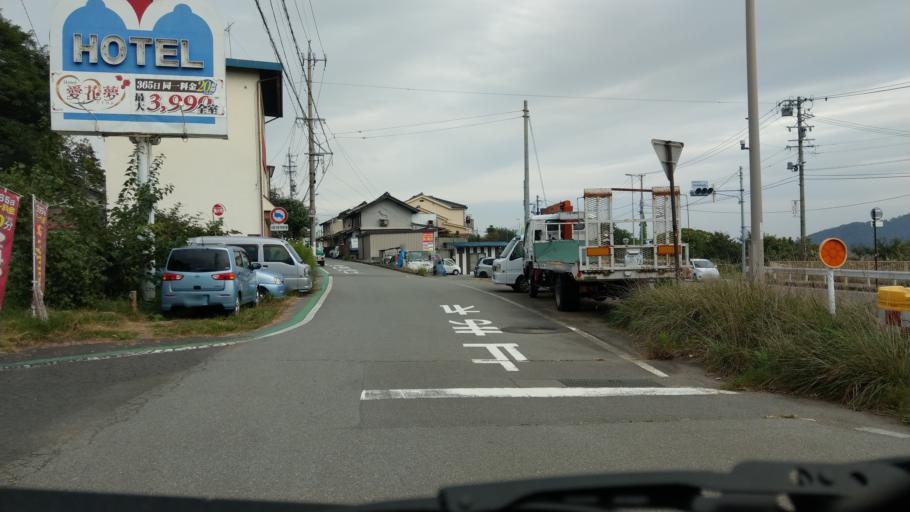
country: JP
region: Nagano
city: Komoro
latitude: 36.3399
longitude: 138.3951
